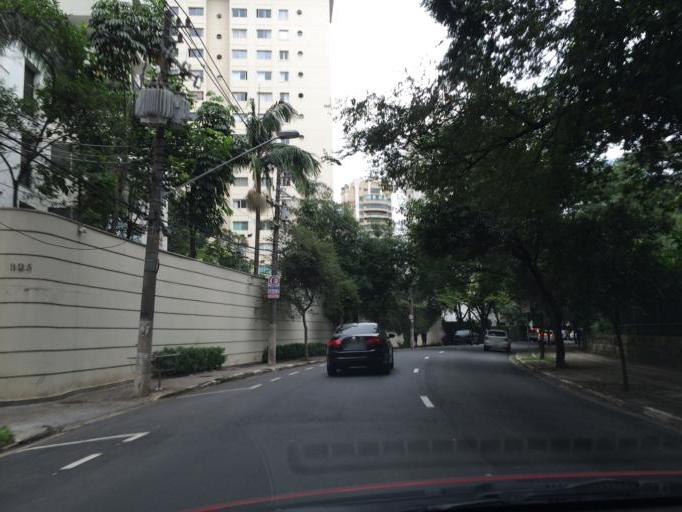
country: BR
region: Sao Paulo
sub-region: Sao Paulo
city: Sao Paulo
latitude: -23.5867
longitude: -46.6867
